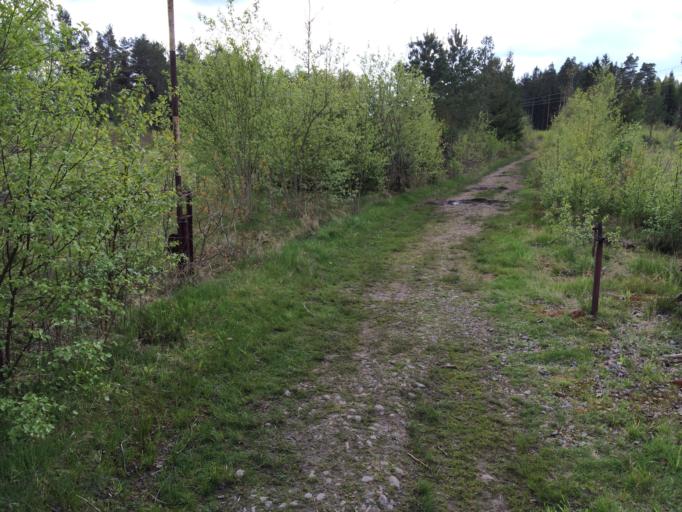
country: SE
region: Vaestra Goetaland
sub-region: Trollhattan
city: Trollhattan
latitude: 58.2258
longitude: 12.2977
